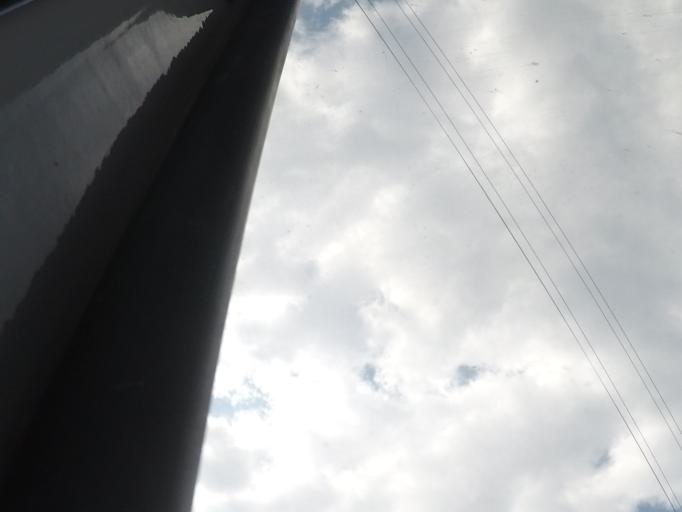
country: PT
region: Setubal
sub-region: Sesimbra
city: Sesimbra
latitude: 38.4624
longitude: -9.0773
